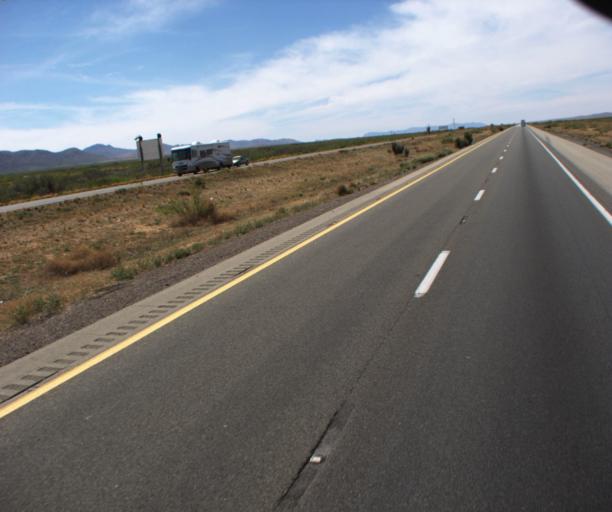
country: US
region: Arizona
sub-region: Cochise County
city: Willcox
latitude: 32.3363
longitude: -109.5390
